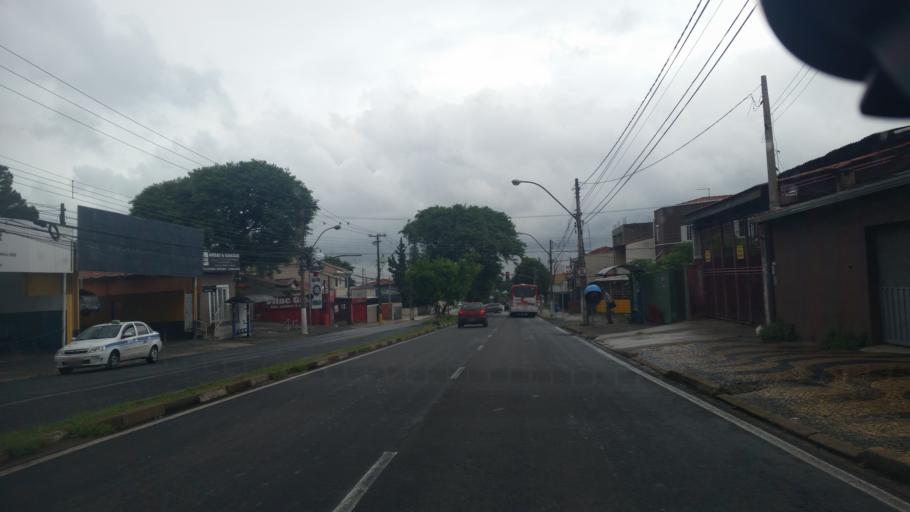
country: BR
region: Sao Paulo
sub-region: Campinas
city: Campinas
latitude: -22.9031
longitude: -47.0828
